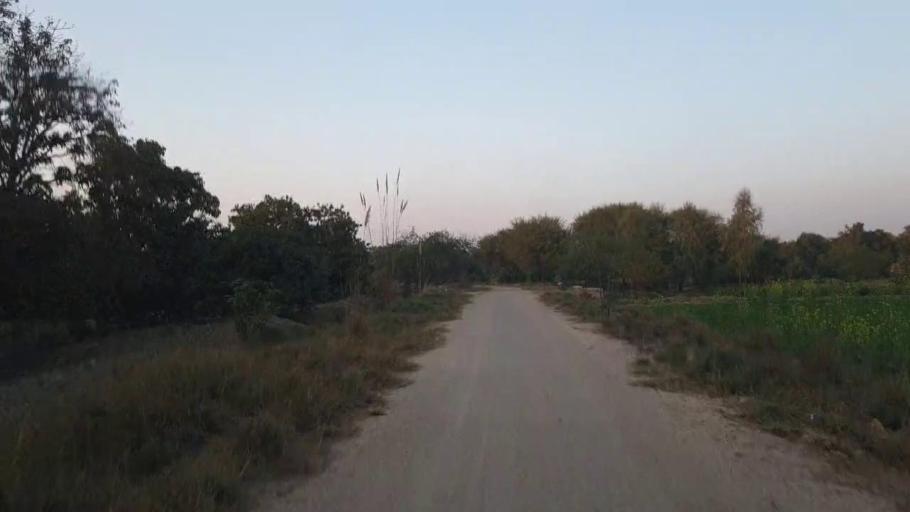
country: PK
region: Sindh
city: Chambar
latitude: 25.4167
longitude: 68.8659
